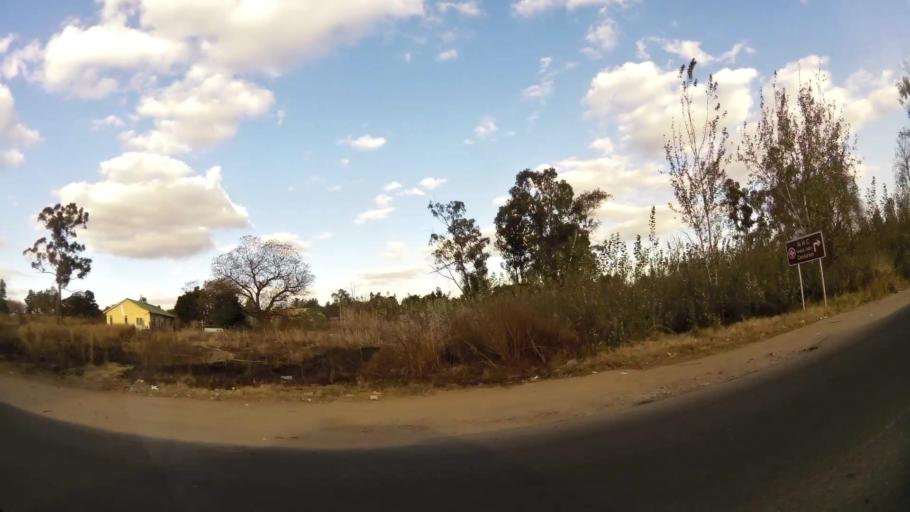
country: ZA
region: Gauteng
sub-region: City of Johannesburg Metropolitan Municipality
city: Midrand
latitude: -25.9560
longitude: 28.1423
